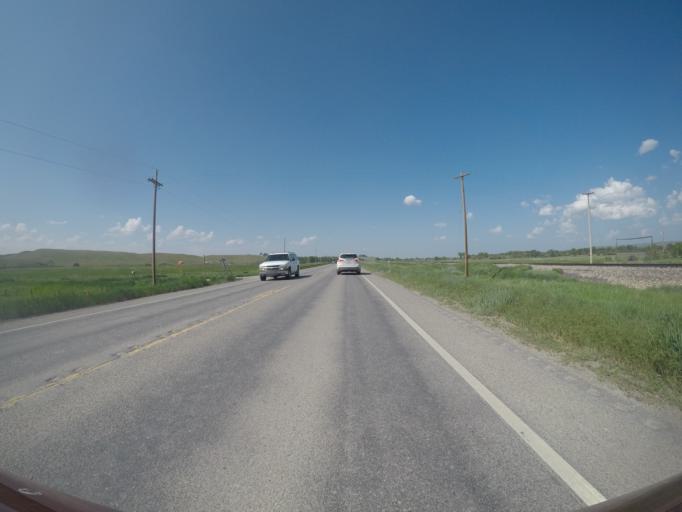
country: US
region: Montana
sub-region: Yellowstone County
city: Laurel
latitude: 45.5662
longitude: -108.8378
